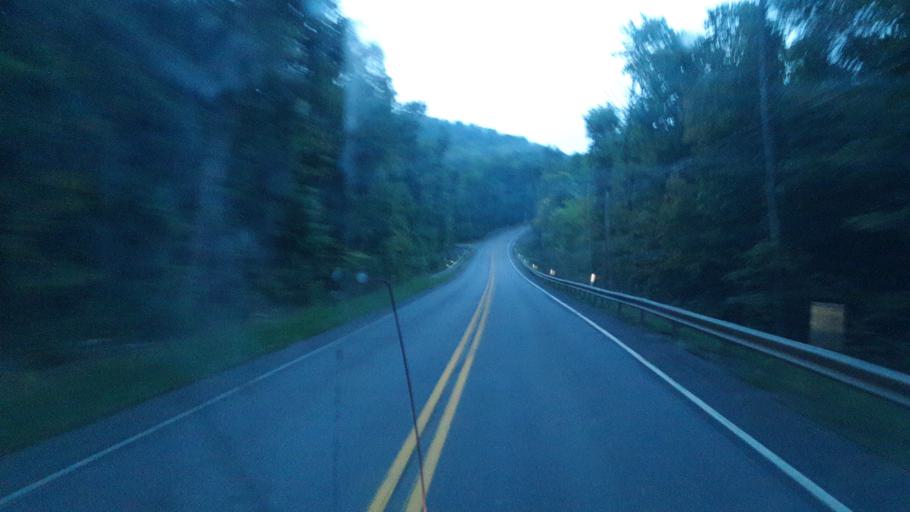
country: US
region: Pennsylvania
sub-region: Clarion County
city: Clarion
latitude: 41.0599
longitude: -79.3219
